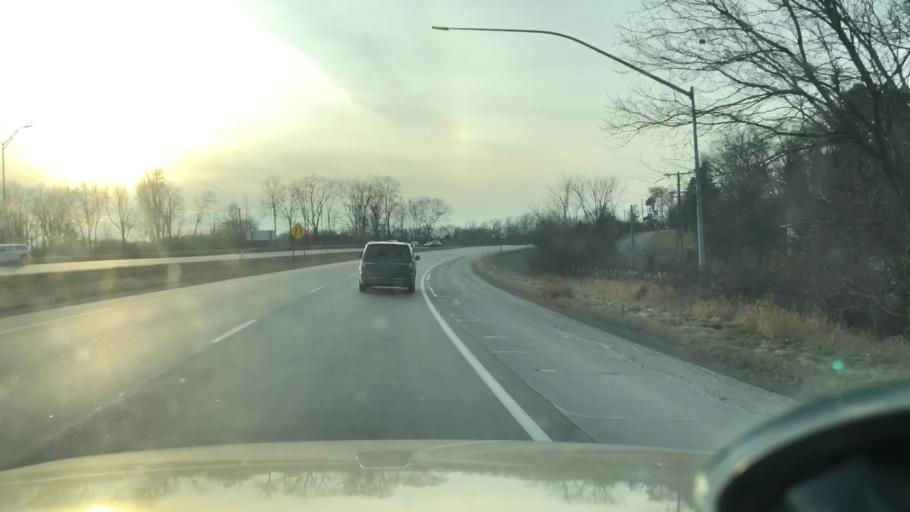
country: US
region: Michigan
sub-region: Jackson County
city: Spring Arbor
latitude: 42.2262
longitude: -84.4795
